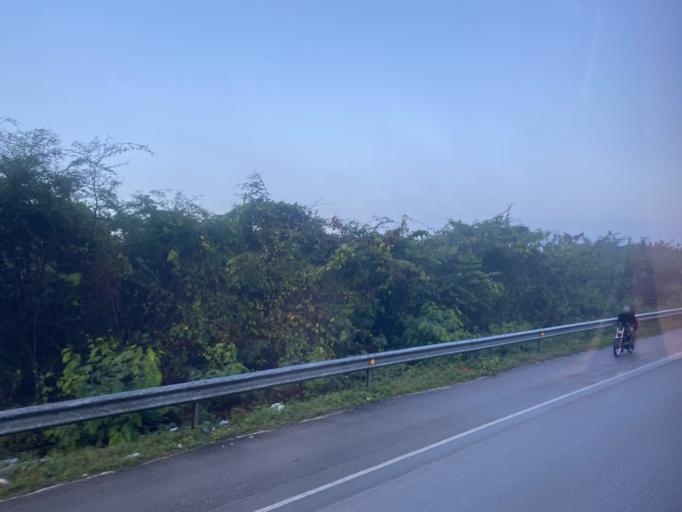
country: DO
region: La Altagracia
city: Otra Banda
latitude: 18.7340
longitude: -68.5075
